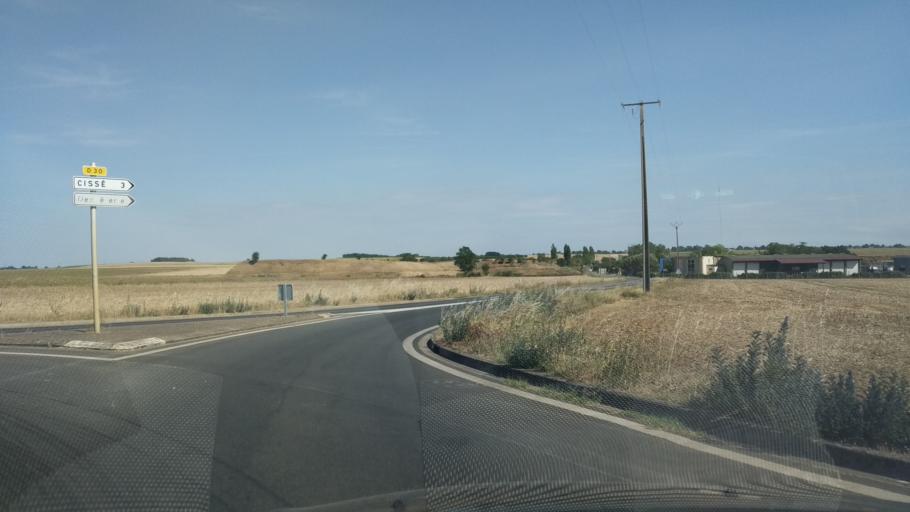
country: FR
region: Poitou-Charentes
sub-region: Departement de la Vienne
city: Cisse
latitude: 46.6644
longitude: 0.2040
